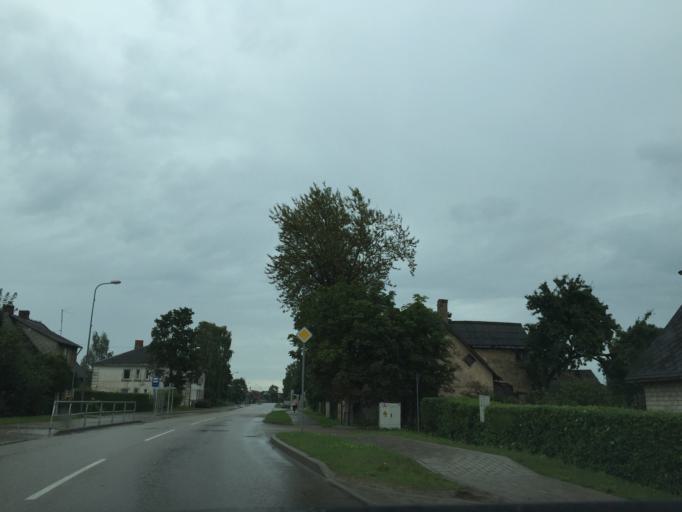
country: LV
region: Jekabpils Rajons
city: Jekabpils
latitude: 56.5021
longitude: 25.8815
